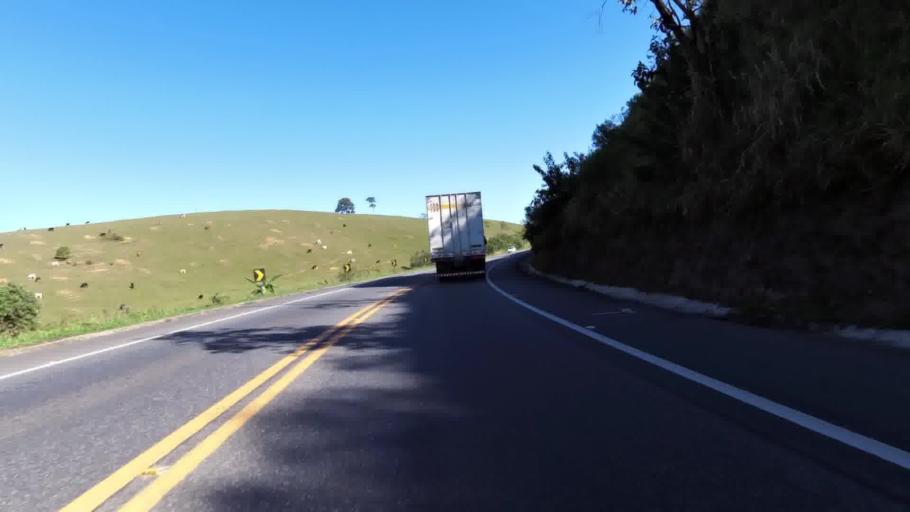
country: BR
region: Espirito Santo
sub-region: Alfredo Chaves
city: Alfredo Chaves
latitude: -20.6936
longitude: -40.6903
